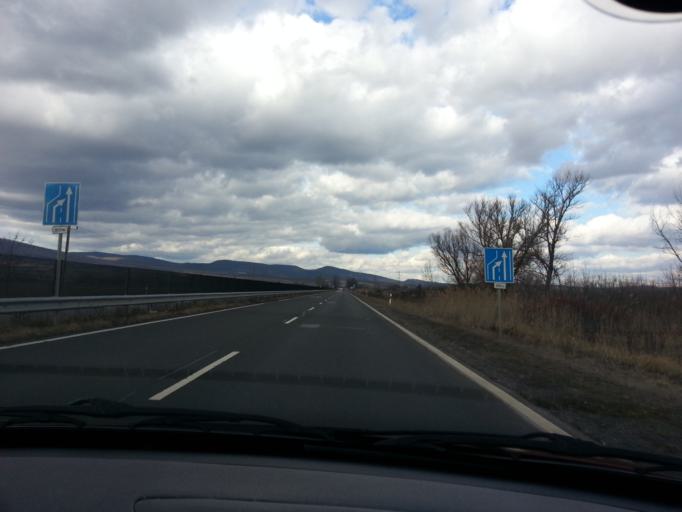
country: HU
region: Nograd
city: Paszto
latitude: 47.9158
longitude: 19.6830
